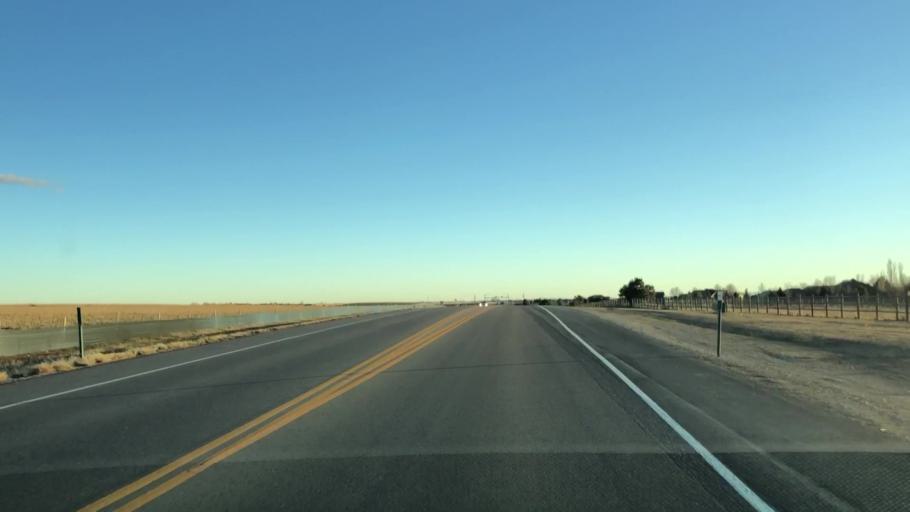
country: US
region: Colorado
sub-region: Weld County
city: Windsor
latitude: 40.4422
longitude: -104.9442
